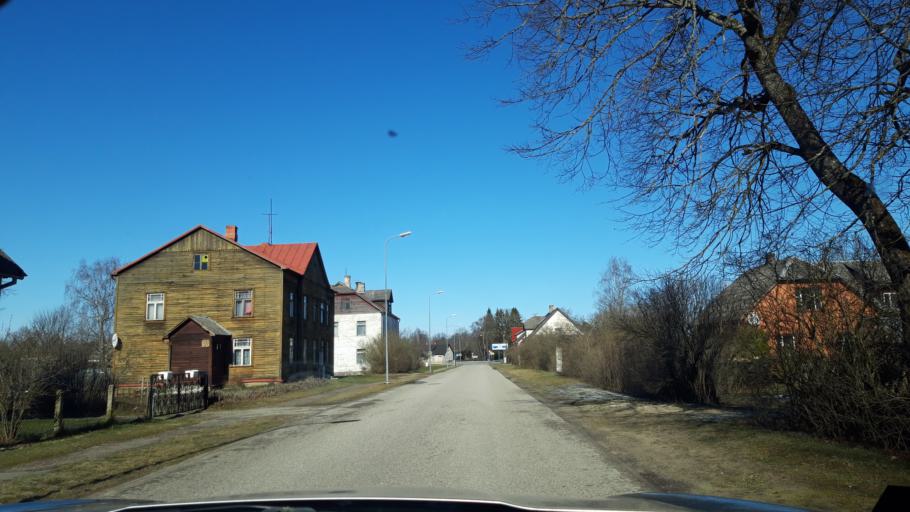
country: LV
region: Strenci
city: Strenci
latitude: 57.6248
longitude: 25.6935
